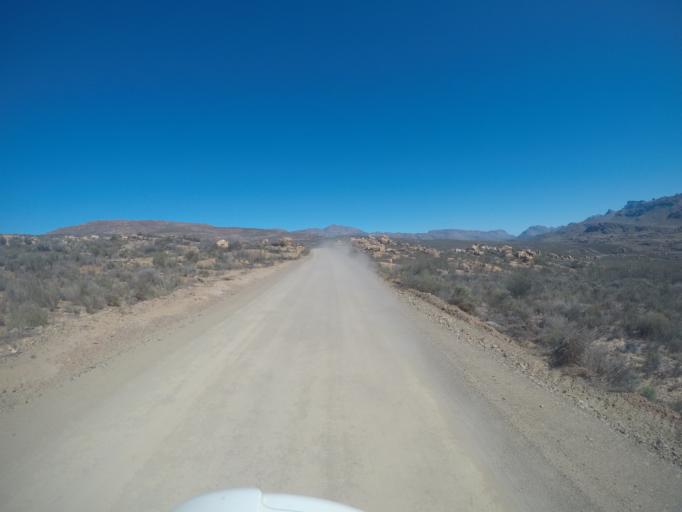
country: ZA
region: Western Cape
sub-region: West Coast District Municipality
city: Clanwilliam
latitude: -32.5051
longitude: 19.2885
